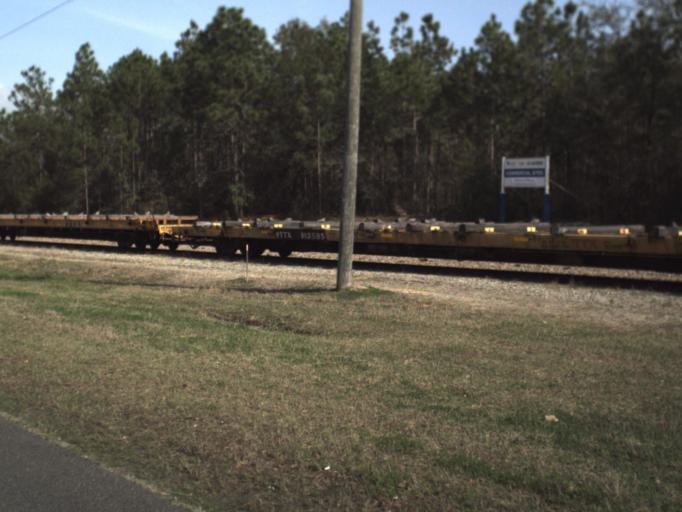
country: US
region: Florida
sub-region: Bay County
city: Hiland Park
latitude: 30.2083
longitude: -85.6142
